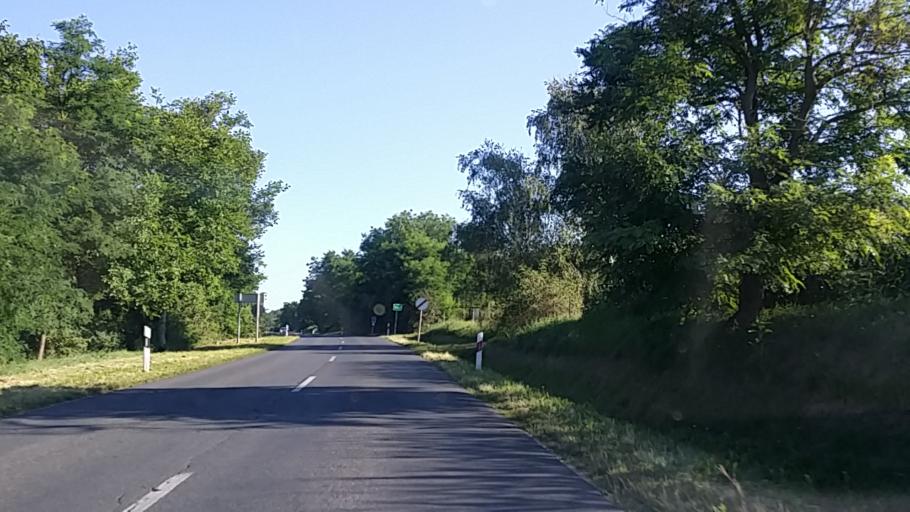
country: HU
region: Zala
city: Cserszegtomaj
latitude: 46.8194
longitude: 17.2023
